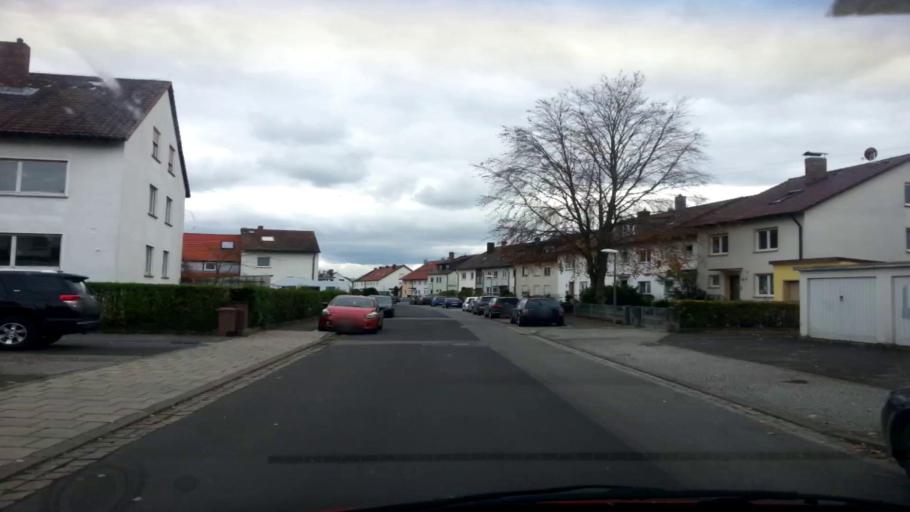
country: DE
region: Bavaria
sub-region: Upper Franconia
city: Bamberg
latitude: 49.8943
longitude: 10.9253
